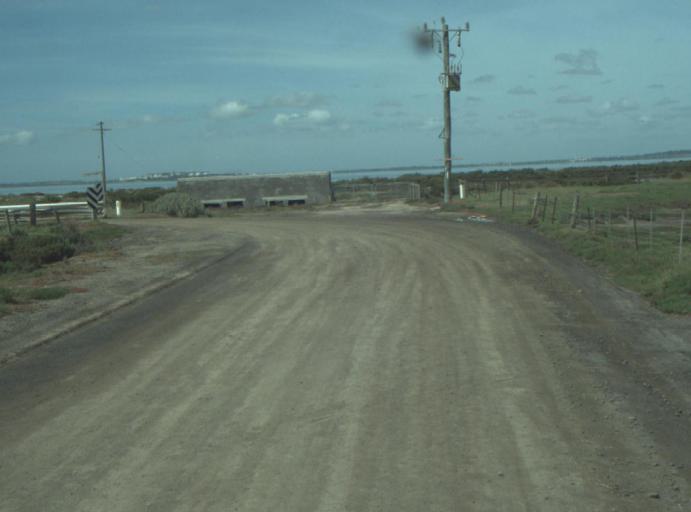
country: AU
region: Victoria
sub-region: Greater Geelong
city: Lara
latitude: -38.0834
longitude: 144.4226
